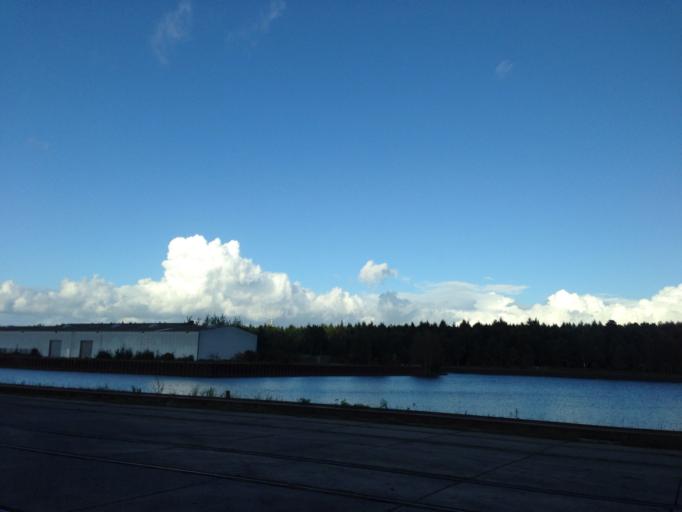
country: DE
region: Lower Saxony
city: Wendisch Evern
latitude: 53.2397
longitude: 10.4835
